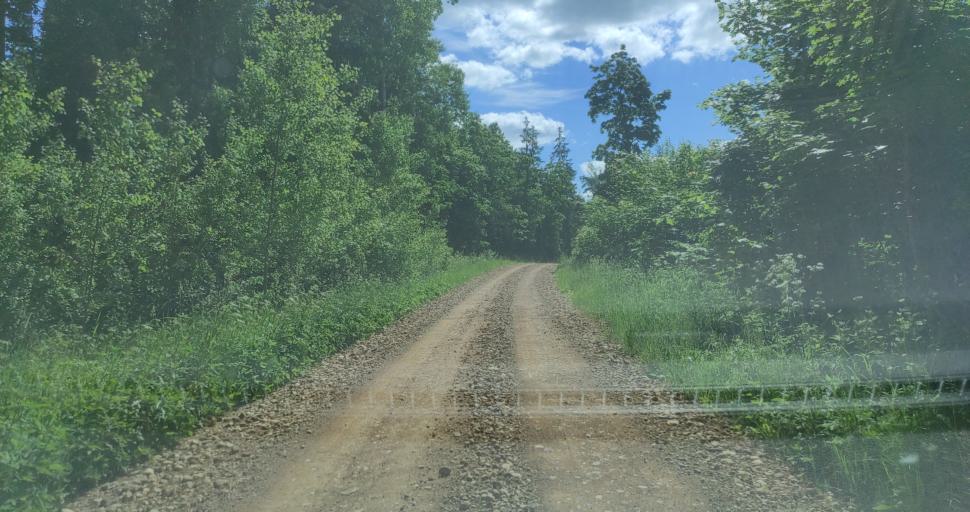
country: LV
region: Alsunga
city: Alsunga
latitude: 56.8875
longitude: 21.7207
